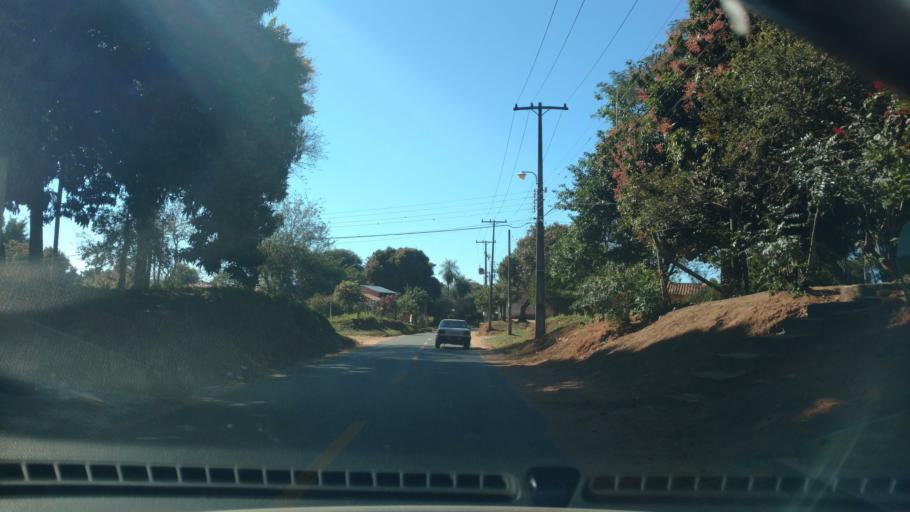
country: PY
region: Central
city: Capiata
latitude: -25.3606
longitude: -57.4175
